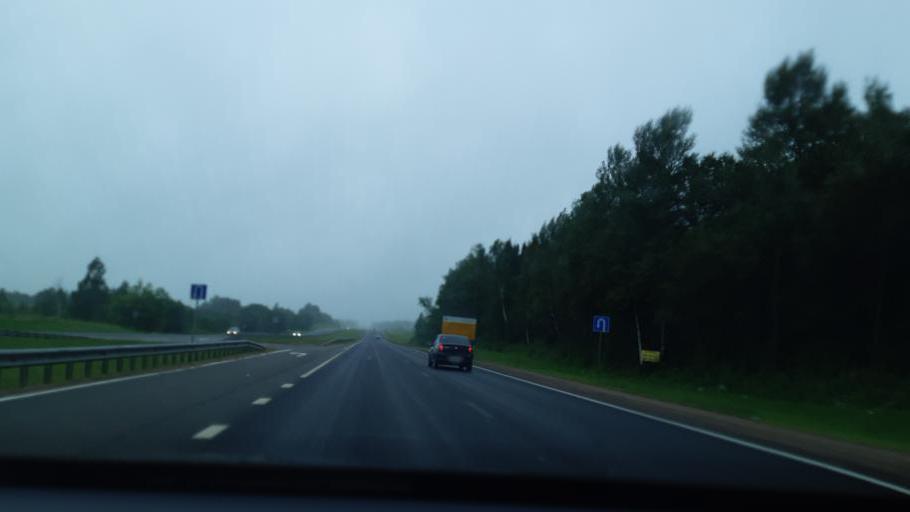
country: RU
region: Smolensk
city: Talashkino
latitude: 54.6225
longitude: 32.1934
